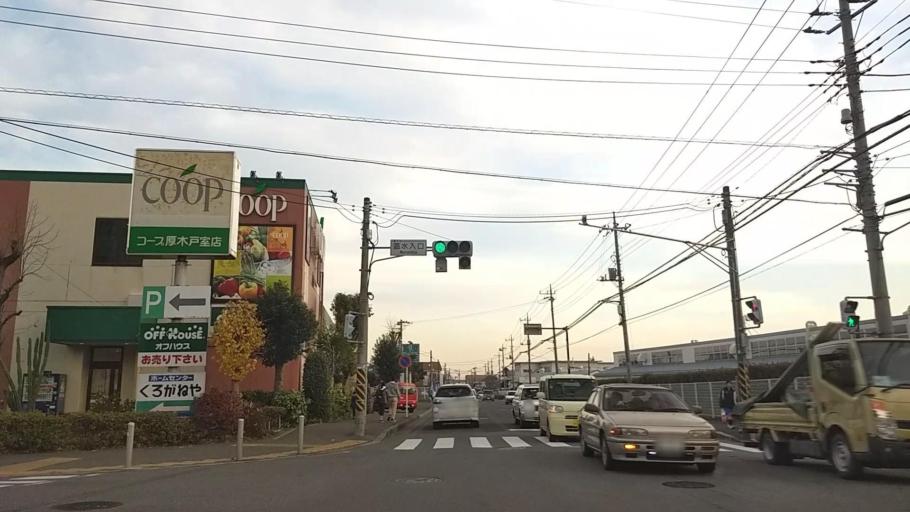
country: JP
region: Kanagawa
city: Atsugi
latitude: 35.4470
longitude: 139.3441
